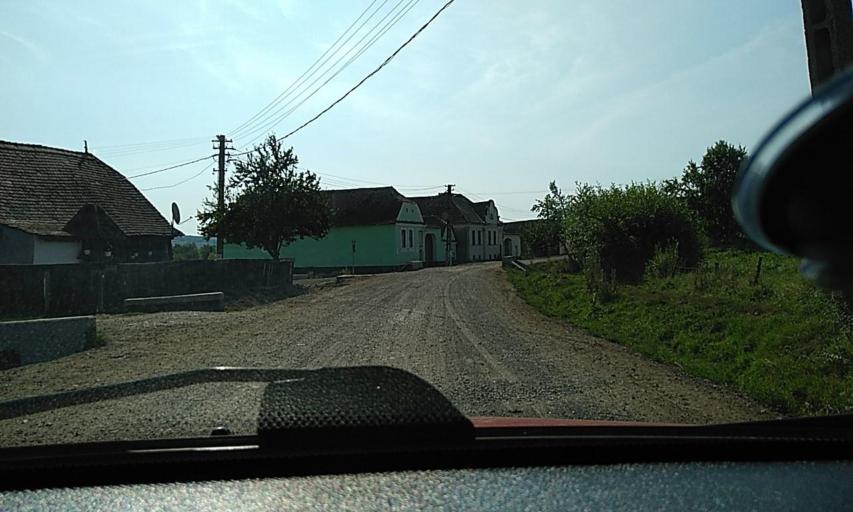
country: RO
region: Brasov
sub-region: Oras Rupea
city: Fiser
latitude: 46.0580
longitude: 25.0961
